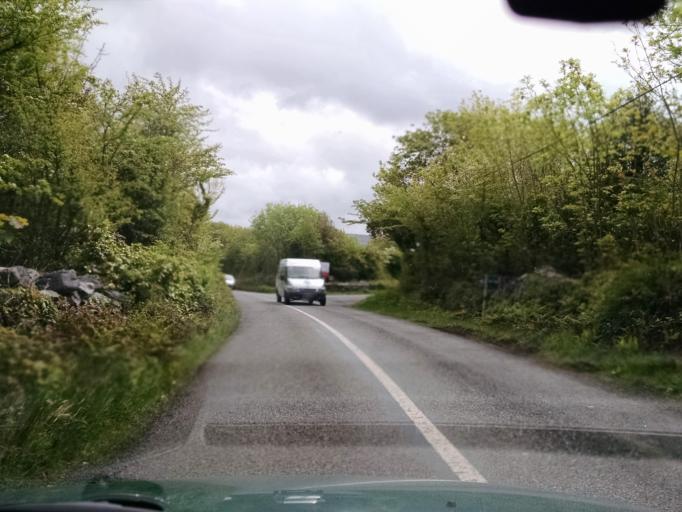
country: IE
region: Connaught
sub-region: County Galway
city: Bearna
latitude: 53.1261
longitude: -9.1798
